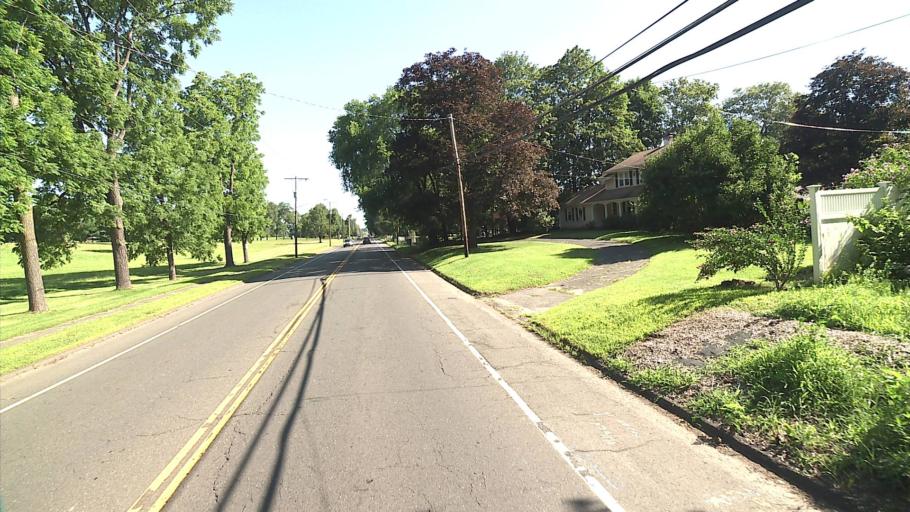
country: US
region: Connecticut
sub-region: New Haven County
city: Cheshire Village
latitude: 41.5191
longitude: -72.8975
